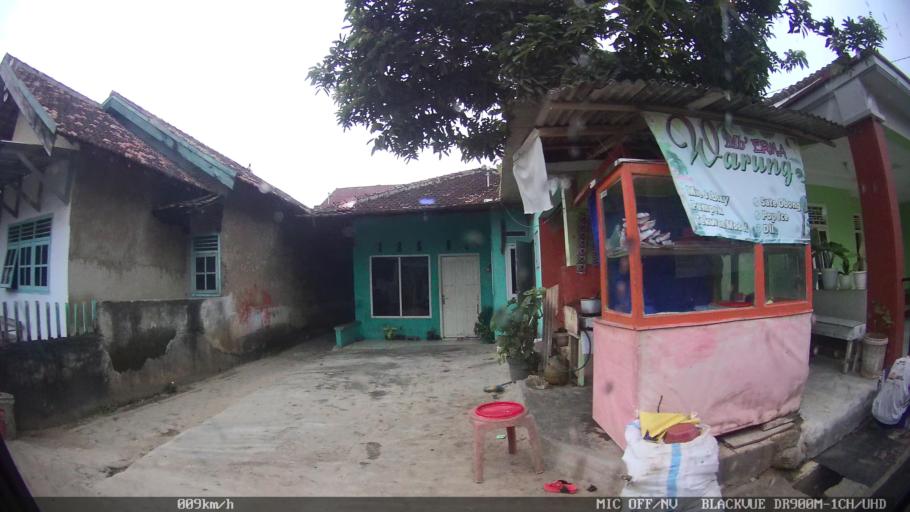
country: ID
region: Lampung
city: Kedaton
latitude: -5.3963
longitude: 105.2796
